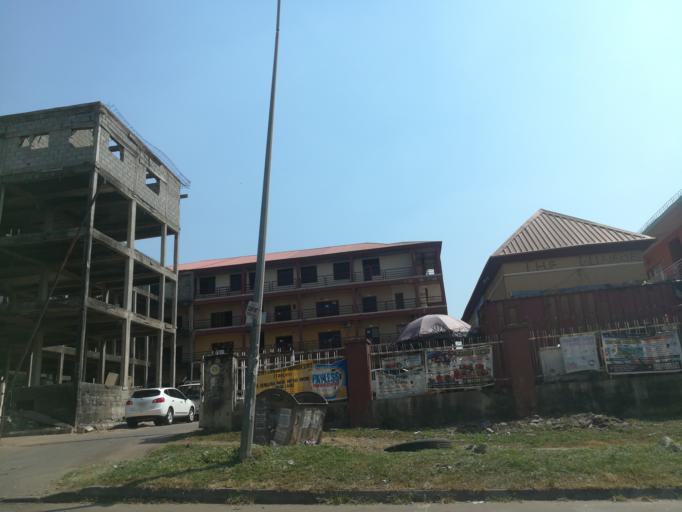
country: NG
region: Abuja Federal Capital Territory
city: Abuja
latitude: 9.0683
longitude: 7.4375
